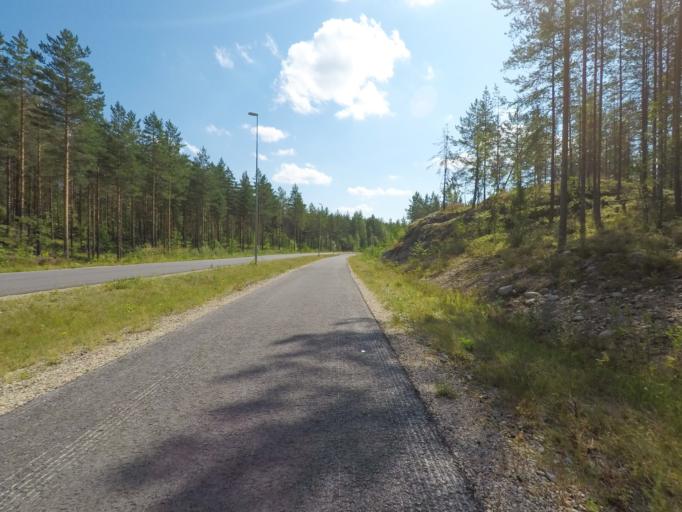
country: FI
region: Southern Savonia
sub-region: Mikkeli
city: Puumala
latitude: 61.5095
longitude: 28.1674
